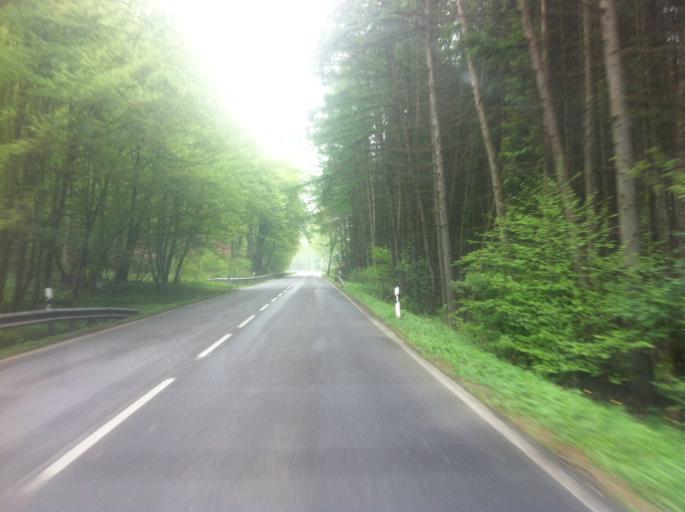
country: DE
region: North Rhine-Westphalia
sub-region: Regierungsbezirk Koln
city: Hennef
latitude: 50.8095
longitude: 7.3397
